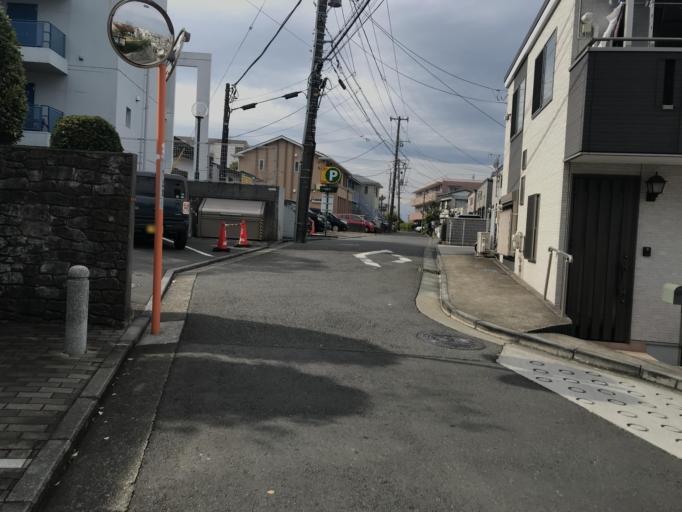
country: JP
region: Kanagawa
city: Yokohama
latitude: 35.4716
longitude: 139.6239
